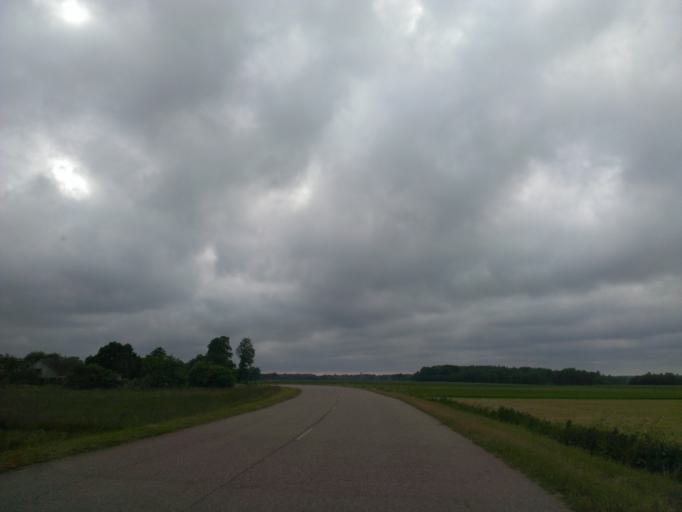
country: LV
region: Aizpute
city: Aizpute
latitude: 56.7247
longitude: 21.4292
